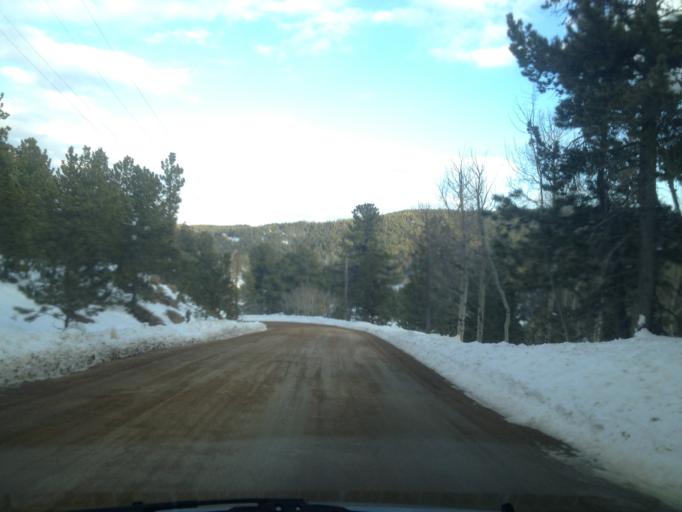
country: US
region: Colorado
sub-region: Boulder County
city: Nederland
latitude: 40.1238
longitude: -105.4574
